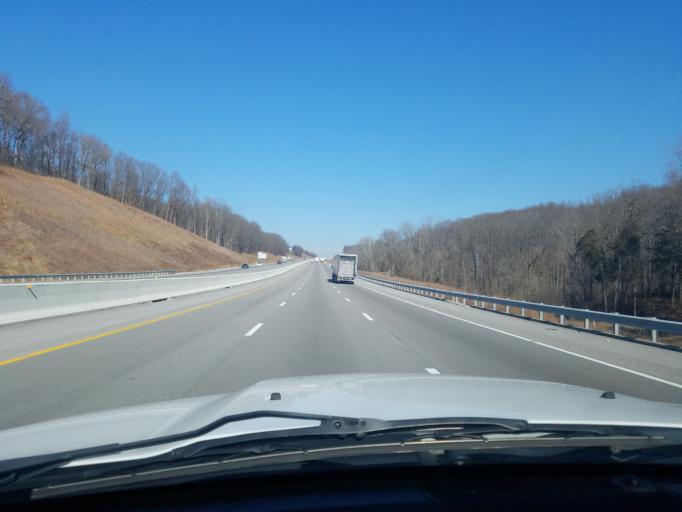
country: US
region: Kentucky
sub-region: Hart County
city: Munfordville
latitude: 37.3105
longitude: -85.9038
